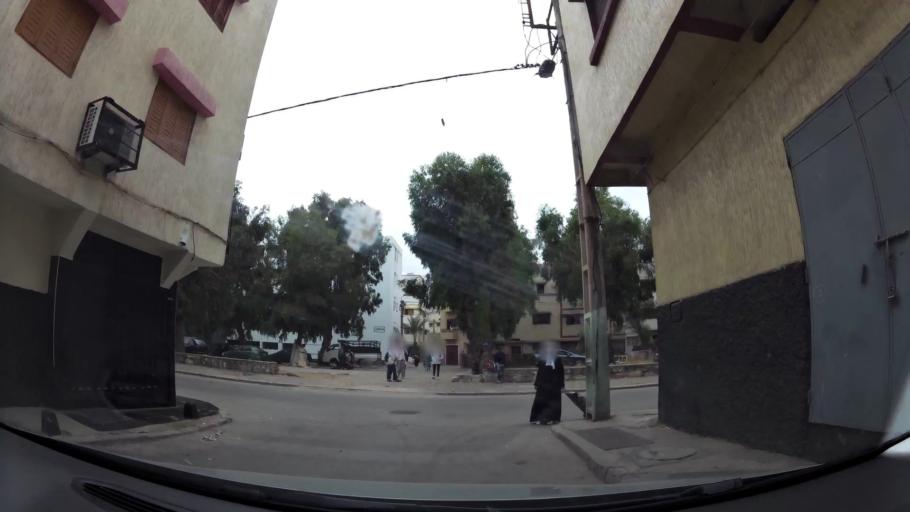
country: MA
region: Rabat-Sale-Zemmour-Zaer
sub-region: Rabat
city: Rabat
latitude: 33.9964
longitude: -6.8686
